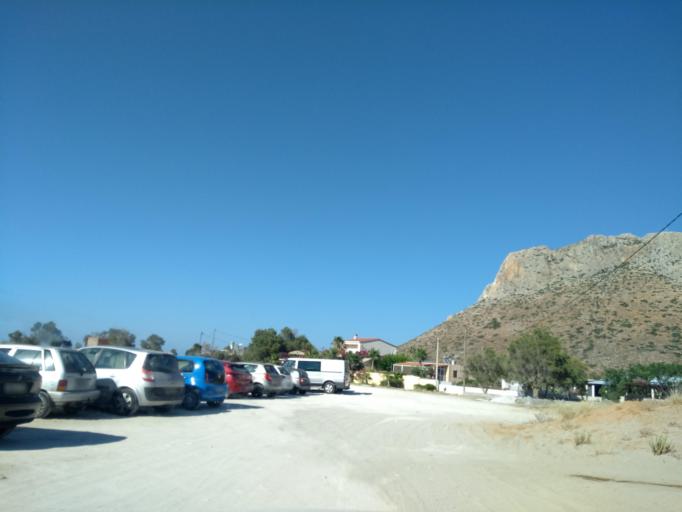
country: GR
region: Crete
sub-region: Nomos Chanias
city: Pithari
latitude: 35.5915
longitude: 24.0910
